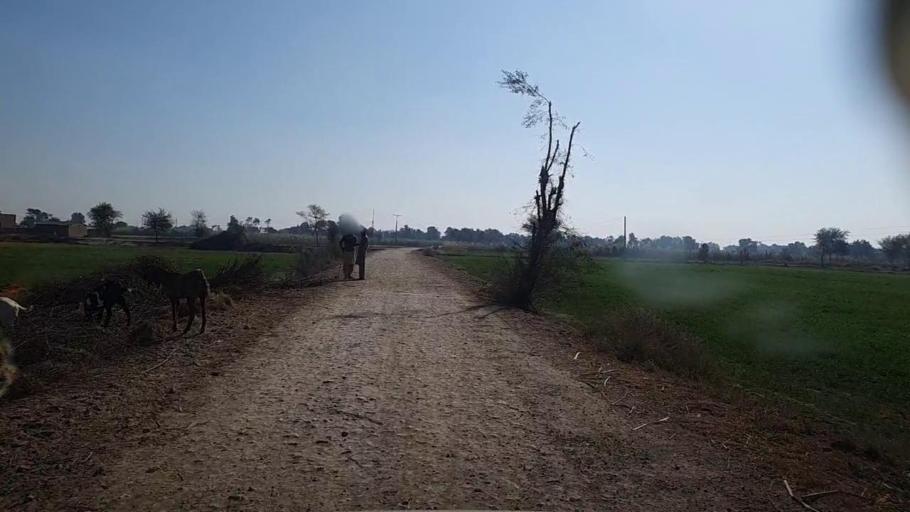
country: PK
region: Sindh
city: Khairpur
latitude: 28.0602
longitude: 69.7440
